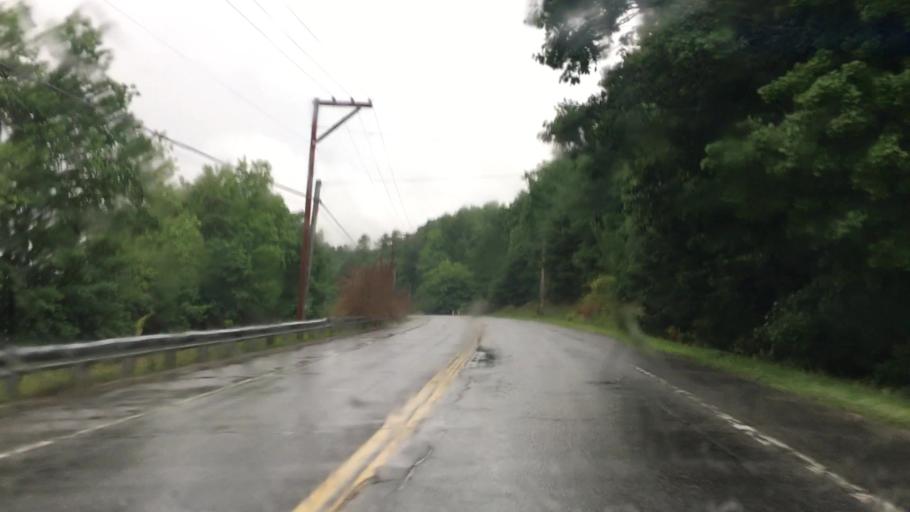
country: US
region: Maine
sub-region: Kennebec County
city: Pittston
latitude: 44.2060
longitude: -69.7651
